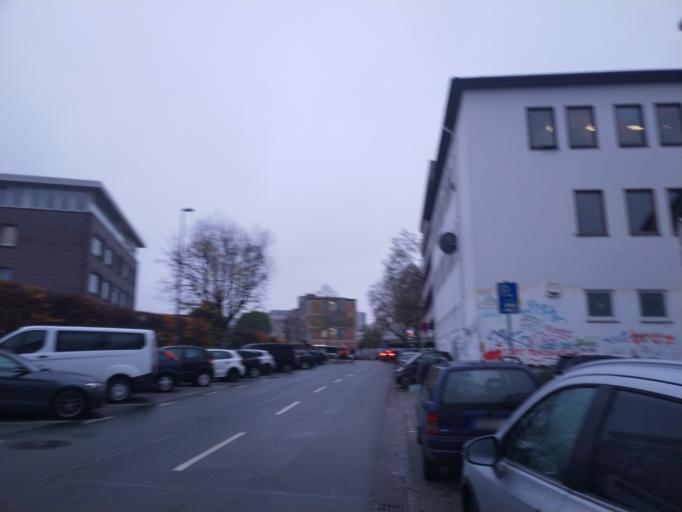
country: DE
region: Bremen
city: Bremen
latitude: 53.0851
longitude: 8.8058
